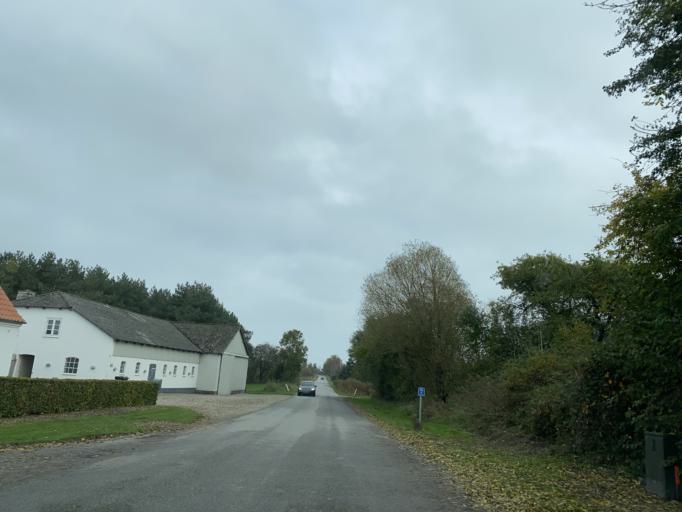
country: DK
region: South Denmark
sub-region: Aabenraa Kommune
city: Lojt Kirkeby
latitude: 55.1576
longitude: 9.4866
